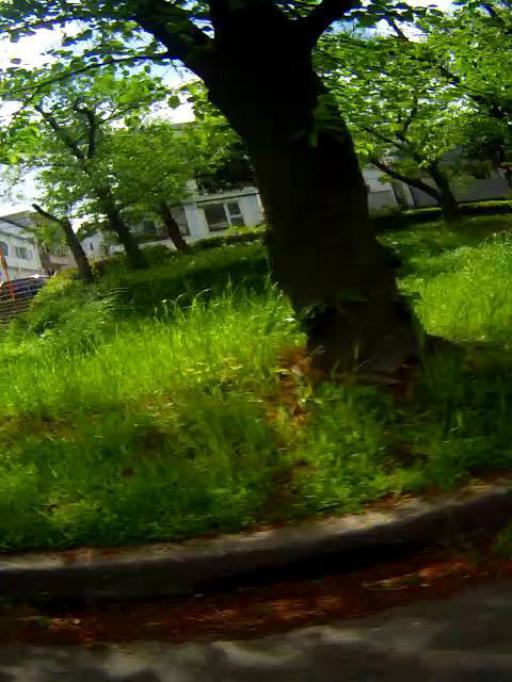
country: JP
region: Osaka
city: Osaka-shi
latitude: 34.6968
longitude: 135.5235
